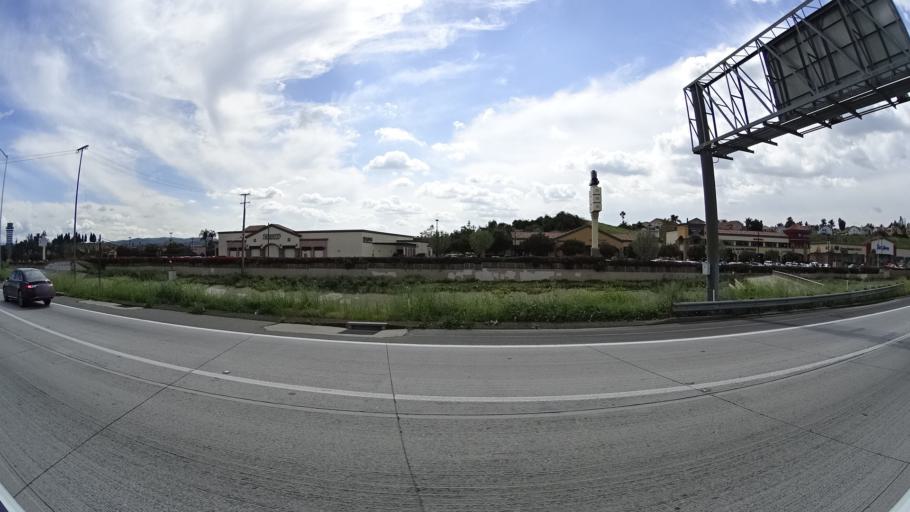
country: US
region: California
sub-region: San Bernardino County
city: Chino Hills
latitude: 34.0044
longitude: -117.7274
